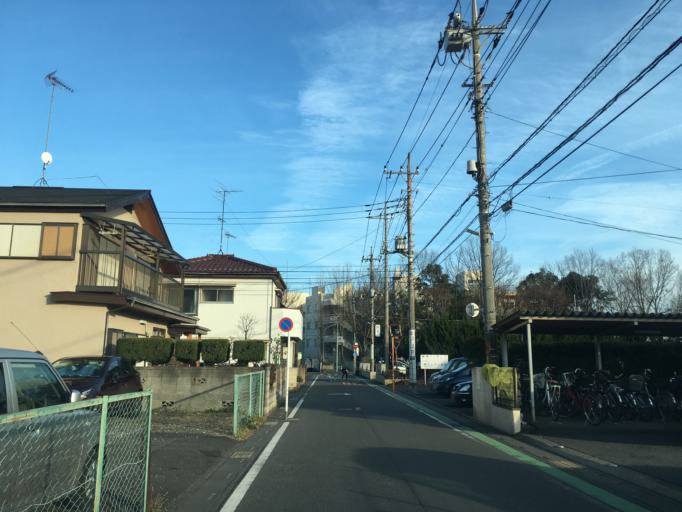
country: JP
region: Saitama
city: Tokorozawa
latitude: 35.8094
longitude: 139.4607
